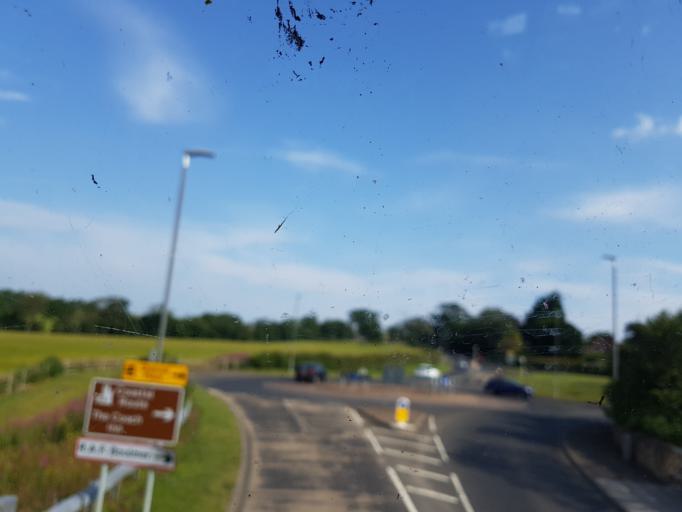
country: GB
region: England
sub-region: Northumberland
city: Alnmouth
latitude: 55.3977
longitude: -1.6349
